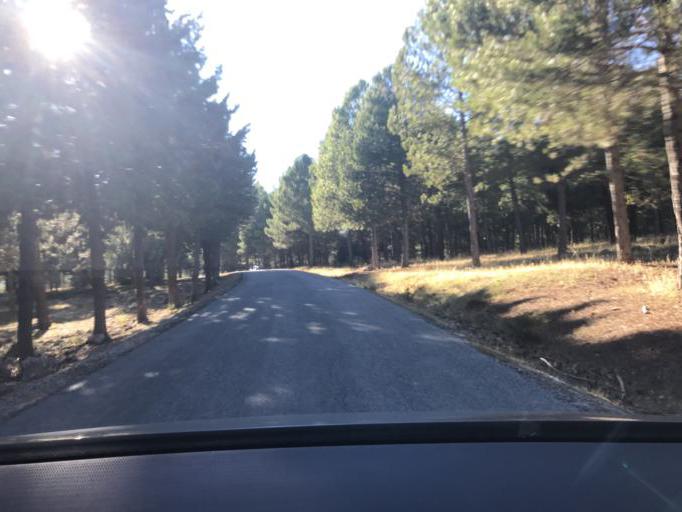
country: ES
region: Andalusia
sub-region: Provincia de Granada
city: Beas de Granada
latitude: 37.3052
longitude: -3.4507
